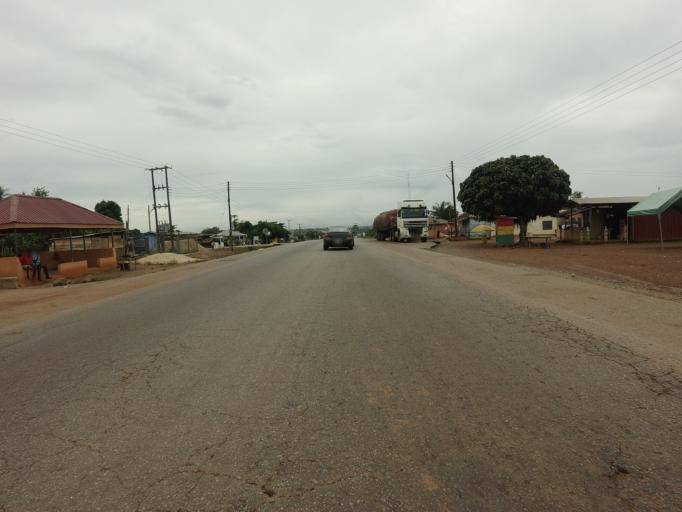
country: GH
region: Eastern
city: Begoro
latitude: 6.3691
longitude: -0.5285
